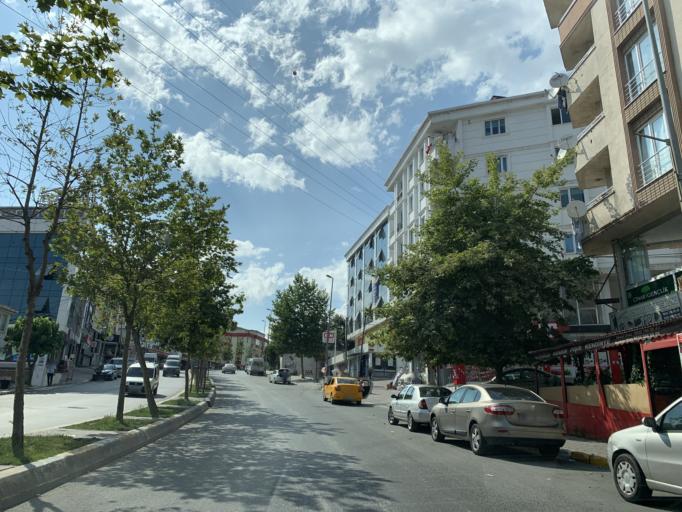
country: TR
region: Istanbul
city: Esenyurt
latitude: 41.0378
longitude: 28.6653
